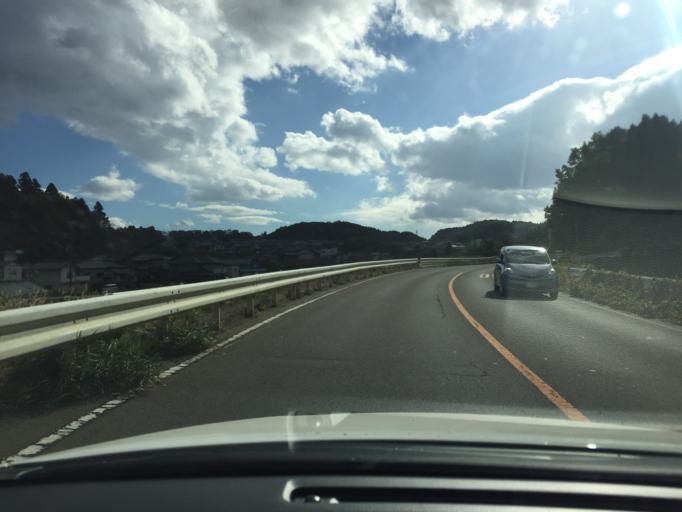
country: JP
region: Fukushima
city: Fukushima-shi
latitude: 37.6725
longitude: 140.4665
